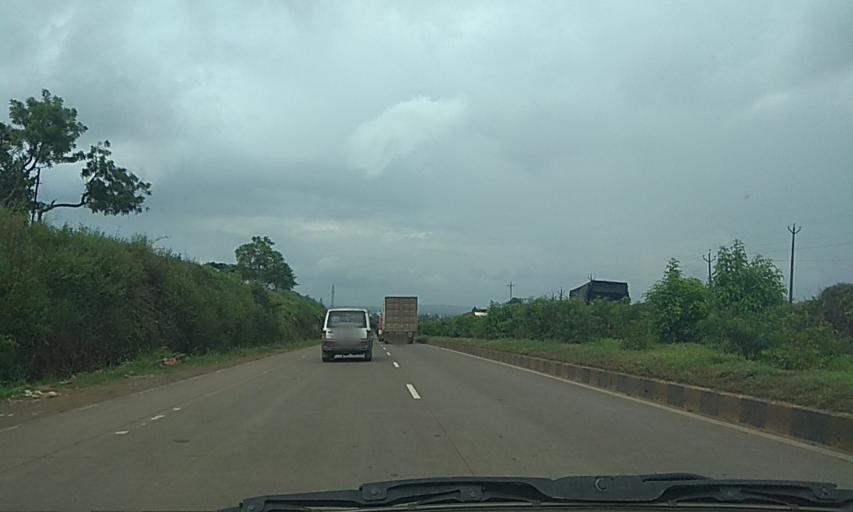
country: IN
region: Maharashtra
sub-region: Kolhapur
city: Kolhapur
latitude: 16.6760
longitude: 74.2703
